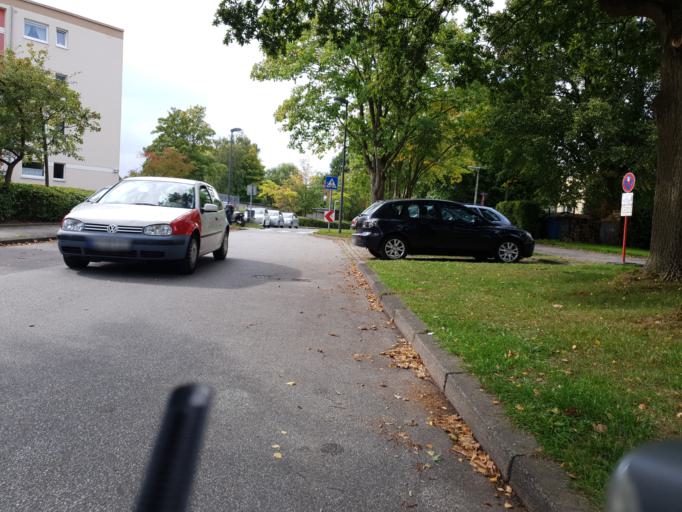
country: DE
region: Schleswig-Holstein
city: Kronshagen
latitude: 54.3596
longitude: 10.0762
